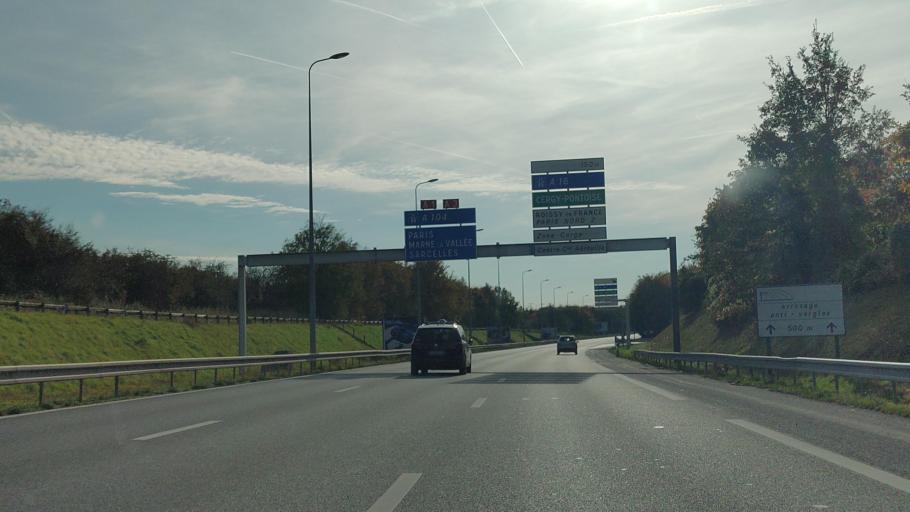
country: FR
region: Ile-de-France
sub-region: Departement du Val-d'Oise
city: Roissy-en-France
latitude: 48.9995
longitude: 2.5195
